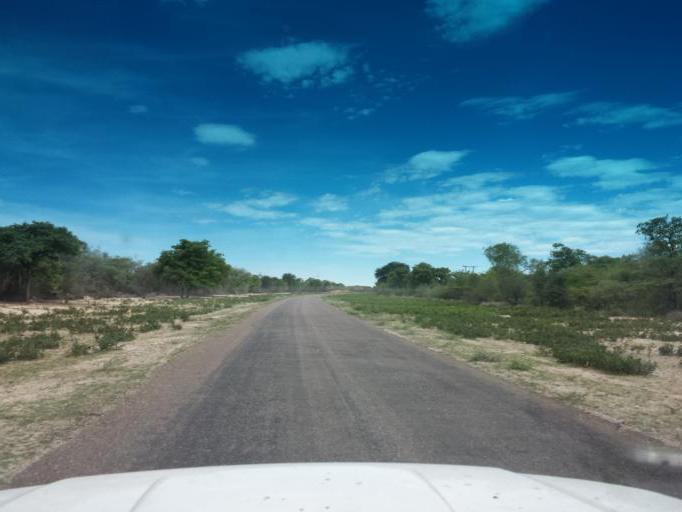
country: BW
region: North West
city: Shakawe
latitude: -18.7113
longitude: 22.1374
